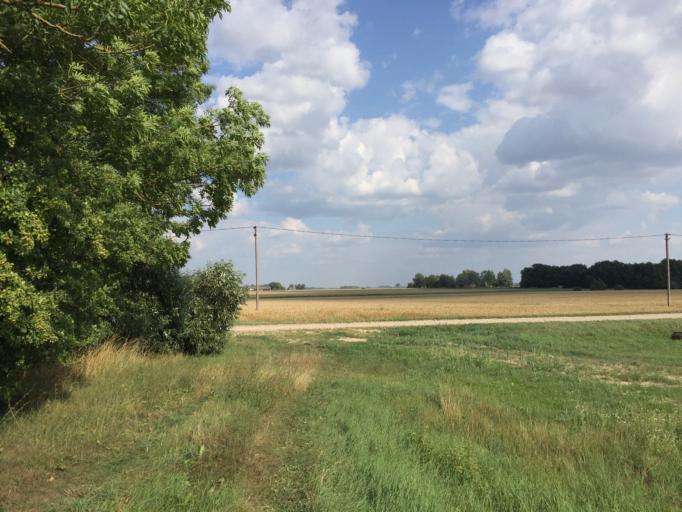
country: LV
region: Jelgava
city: Jelgava
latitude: 56.4813
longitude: 23.7586
